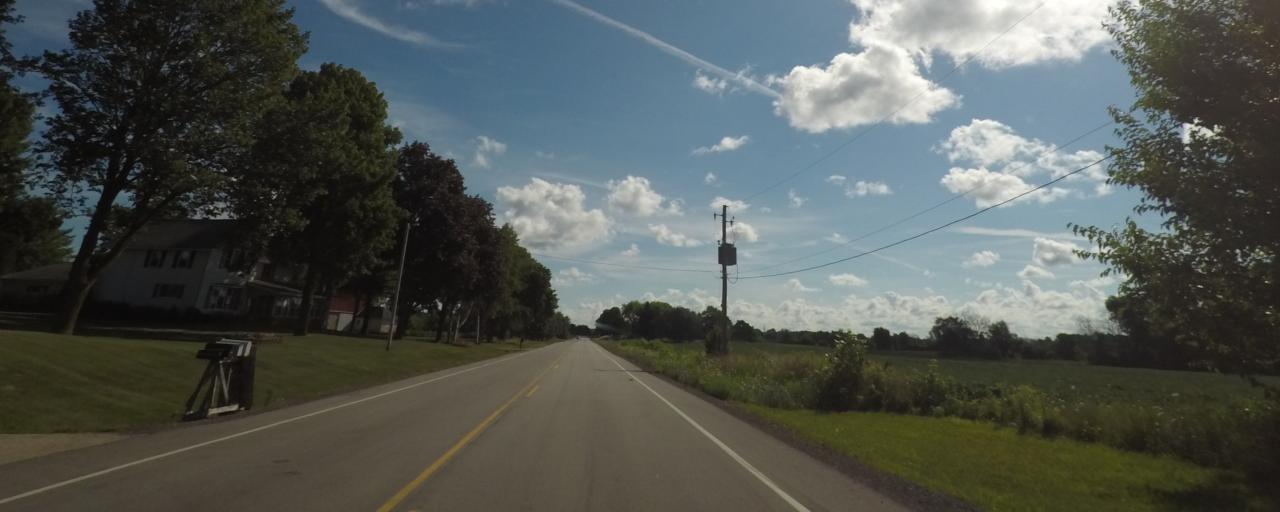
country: US
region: Wisconsin
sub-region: Jefferson County
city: Ixonia
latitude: 43.0722
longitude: -88.5801
